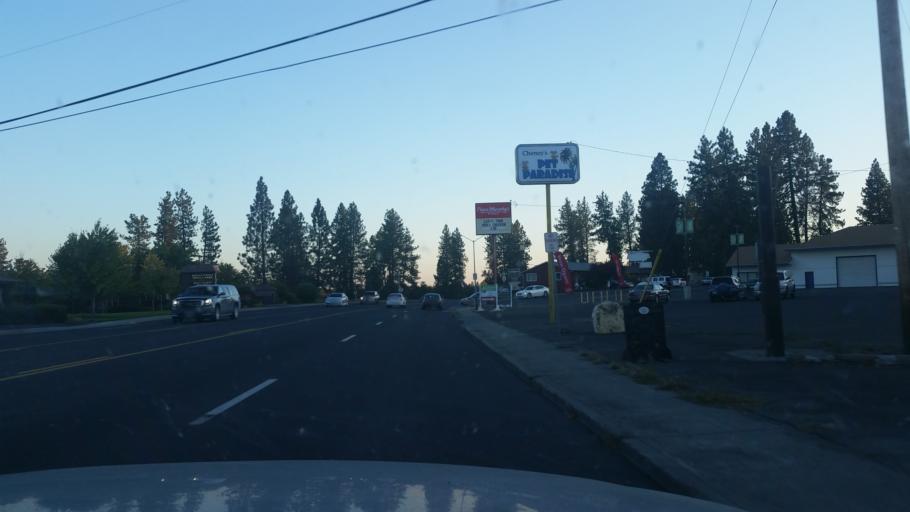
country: US
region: Washington
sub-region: Spokane County
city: Cheney
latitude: 47.4980
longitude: -117.5649
